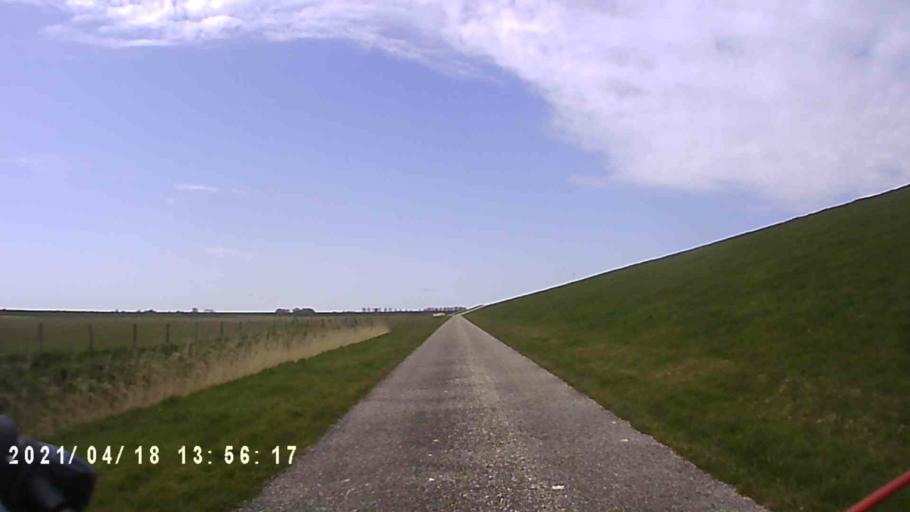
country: NL
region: Friesland
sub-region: Gemeente Dongeradeel
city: Anjum
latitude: 53.4004
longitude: 6.1066
